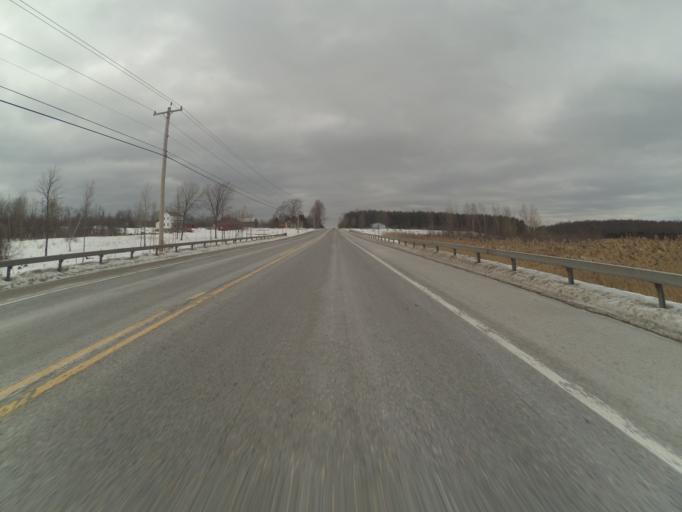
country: US
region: New York
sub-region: St. Lawrence County
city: Potsdam
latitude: 44.7135
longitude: -74.9211
